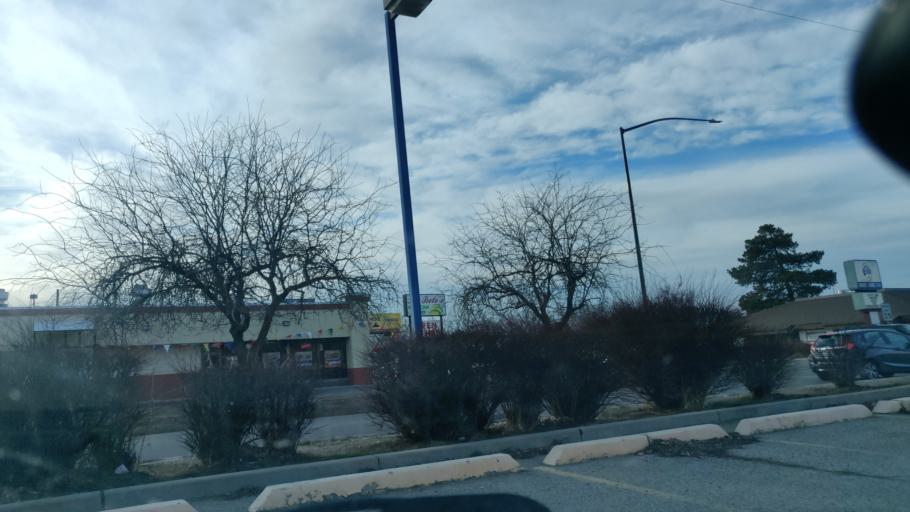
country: US
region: Idaho
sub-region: Ada County
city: Garden City
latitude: 43.6188
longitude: -116.2634
